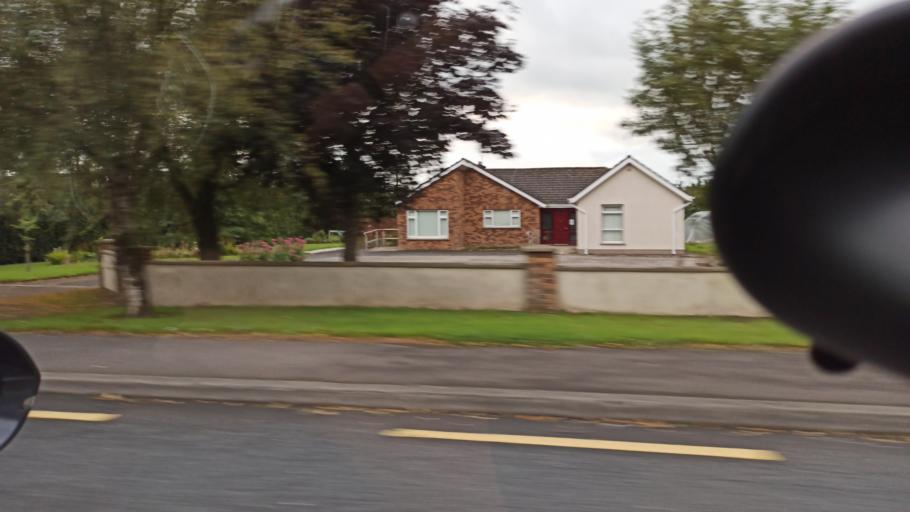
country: IE
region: Munster
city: Thurles
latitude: 52.6907
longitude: -7.8117
